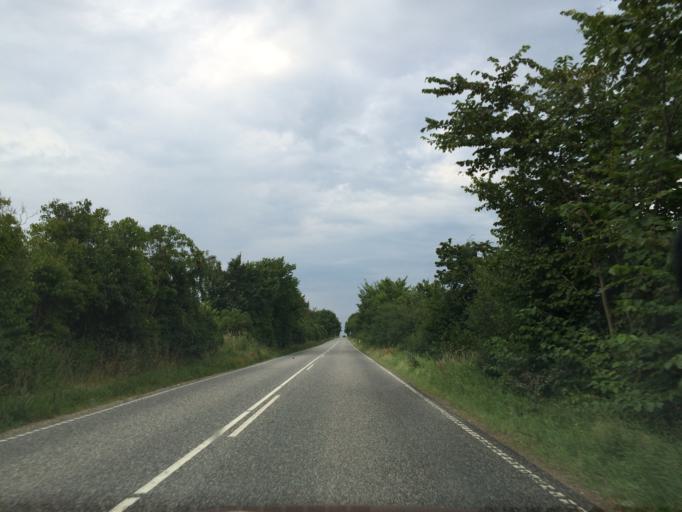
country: DK
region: South Denmark
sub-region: Sonderborg Kommune
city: Broager
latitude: 54.9253
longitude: 9.6847
